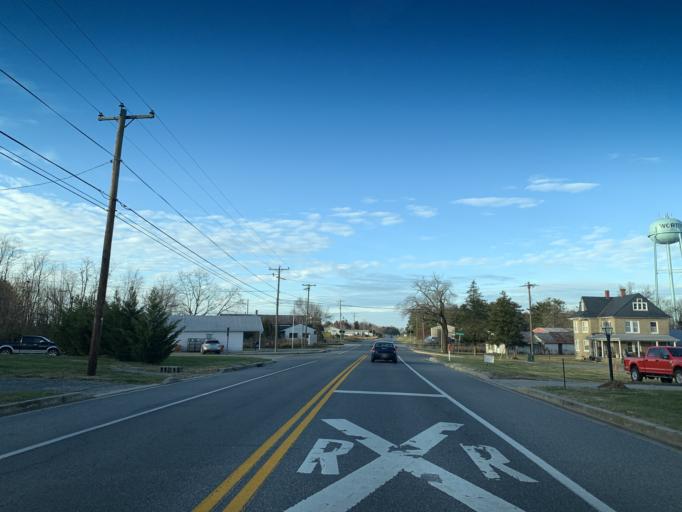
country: US
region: Maryland
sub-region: Kent County
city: Chestertown
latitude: 39.2738
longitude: -76.0918
